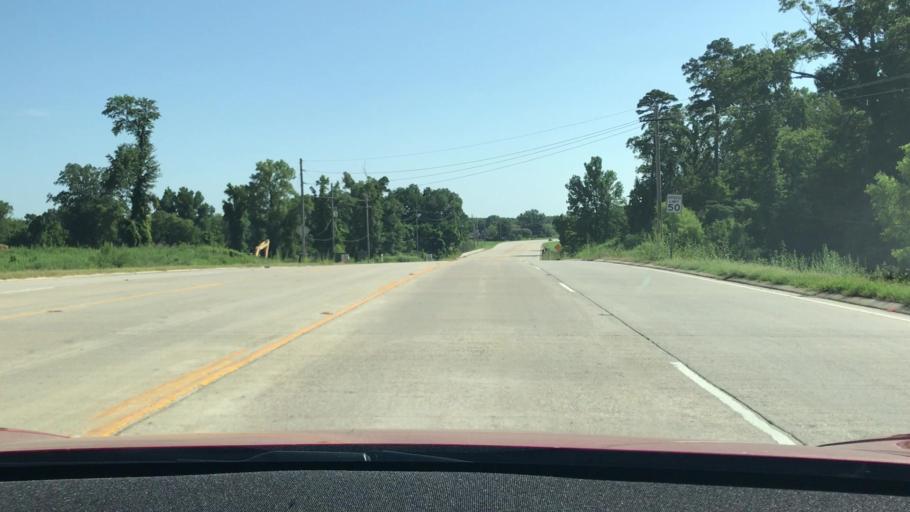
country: US
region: Louisiana
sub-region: Bossier Parish
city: Bossier City
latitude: 32.3953
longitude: -93.7248
